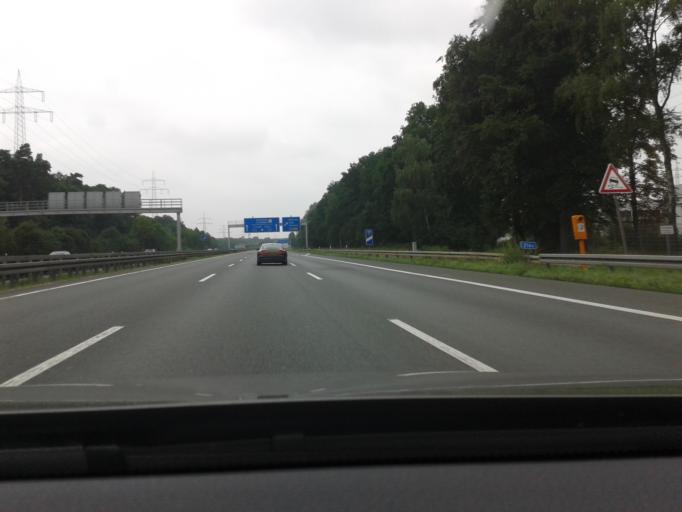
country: DE
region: Lower Saxony
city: Isernhagen Farster Bauerschaft
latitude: 52.4071
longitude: 9.8595
